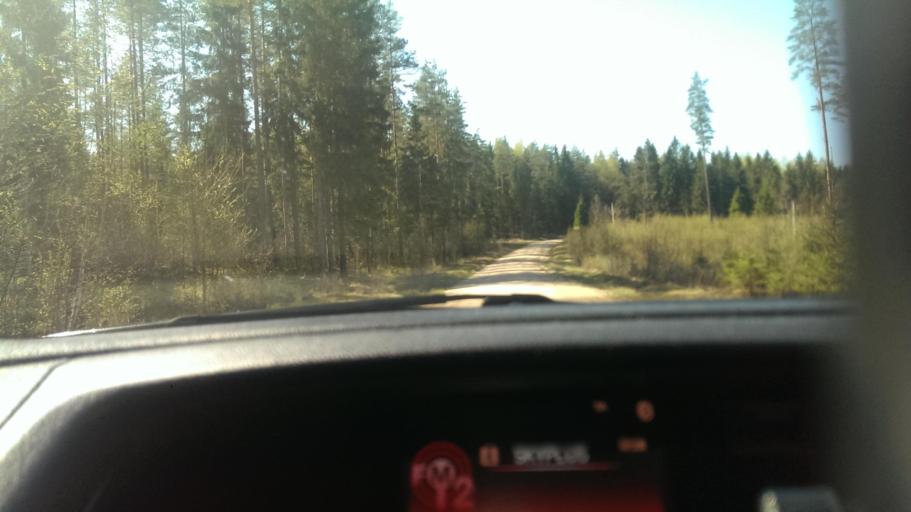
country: EE
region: Vorumaa
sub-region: Antsla vald
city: Vana-Antsla
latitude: 57.9973
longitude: 26.7231
